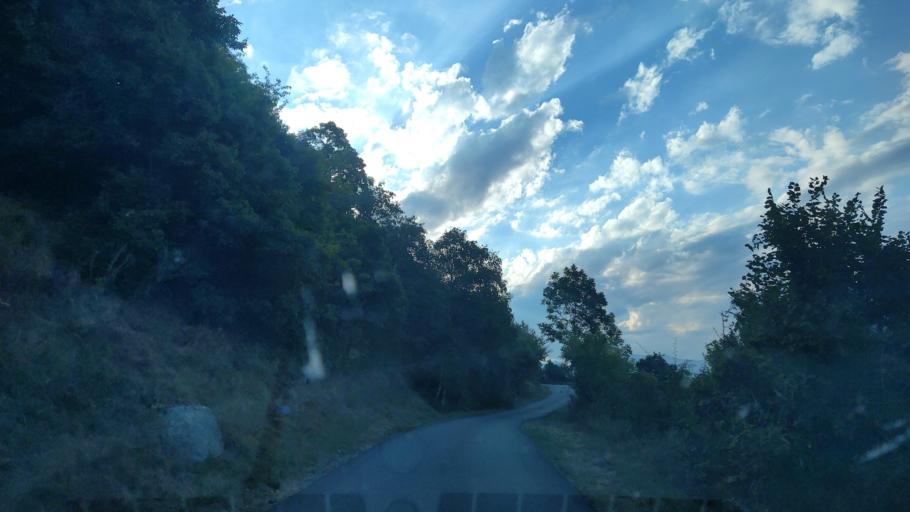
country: FR
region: Rhone-Alpes
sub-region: Departement de la Savoie
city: Val Thorens
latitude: 45.2121
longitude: 6.5651
